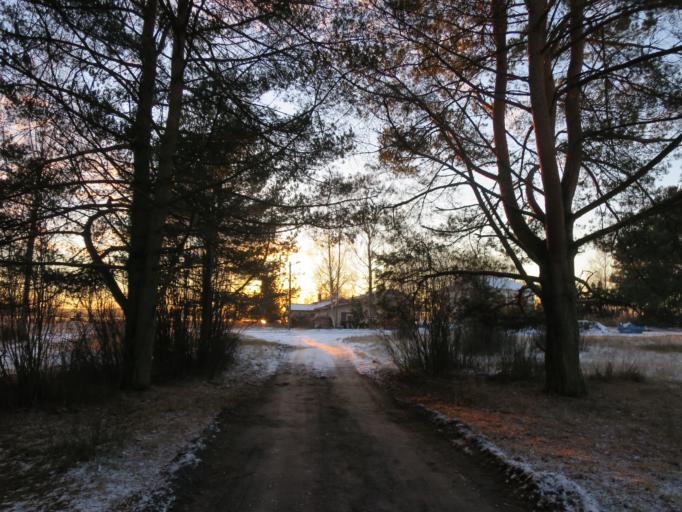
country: LV
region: Riga
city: Bergi
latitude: 56.9790
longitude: 24.3032
